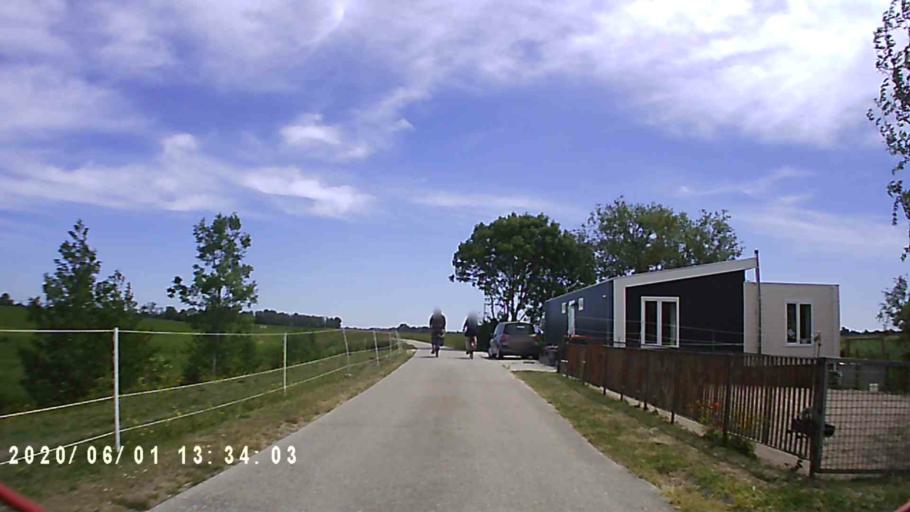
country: NL
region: Friesland
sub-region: Gemeente Littenseradiel
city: Wommels
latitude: 53.0903
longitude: 5.5730
